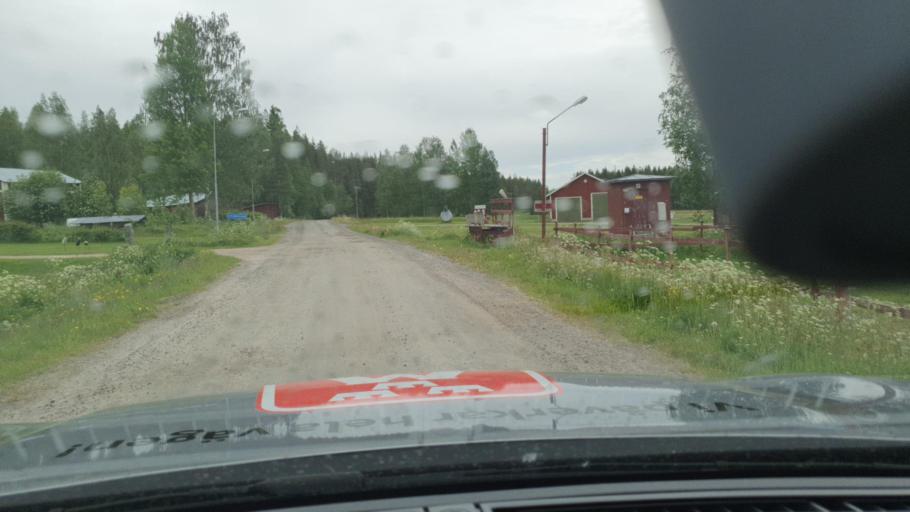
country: SE
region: Norrbotten
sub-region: Kalix Kommun
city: Rolfs
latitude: 66.0426
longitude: 23.0479
